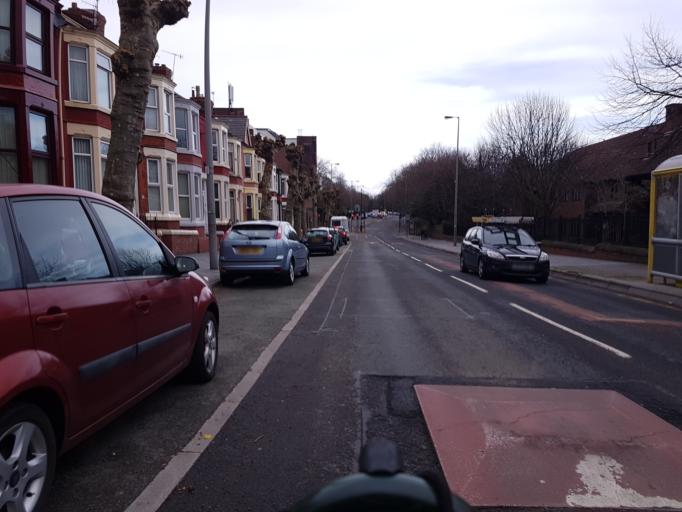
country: GB
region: England
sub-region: Liverpool
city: Liverpool
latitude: 53.3801
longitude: -2.9587
